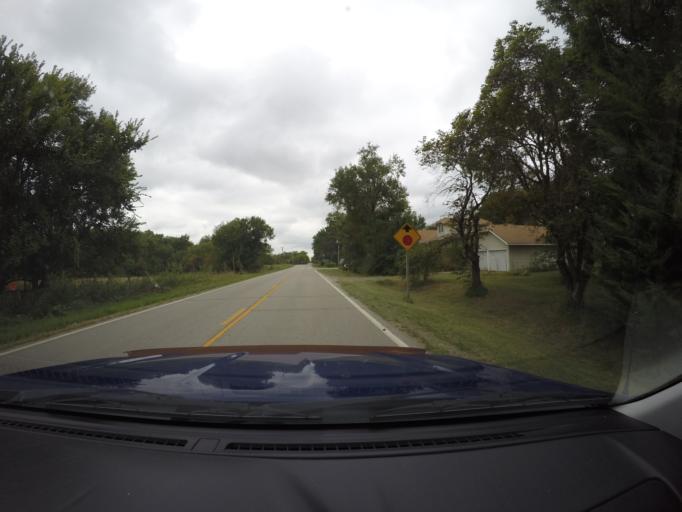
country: US
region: Kansas
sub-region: Morris County
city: Council Grove
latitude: 38.8412
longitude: -96.5916
